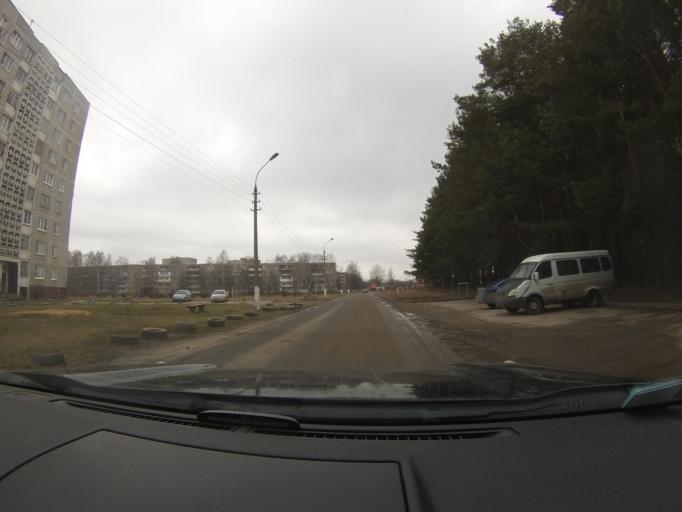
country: RU
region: Moskovskaya
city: Peski
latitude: 55.2771
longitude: 38.7541
